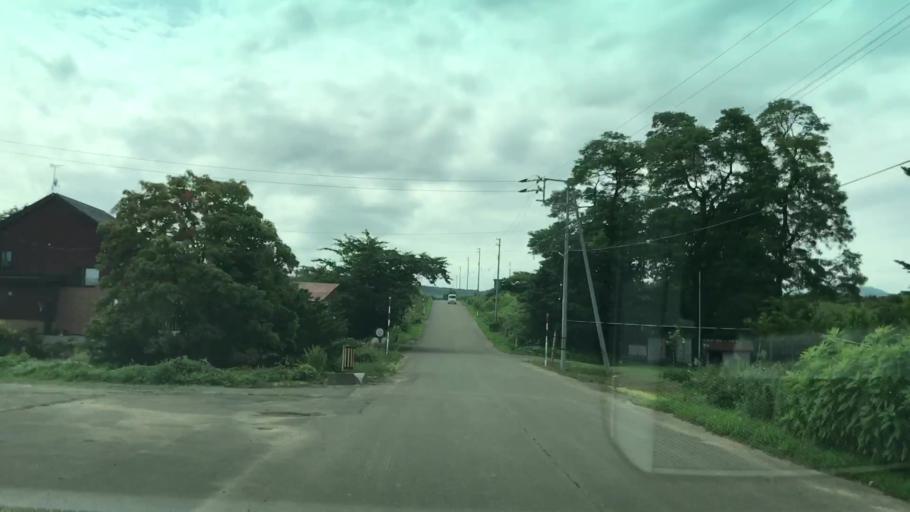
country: JP
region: Hokkaido
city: Yoichi
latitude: 43.1773
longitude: 140.8383
